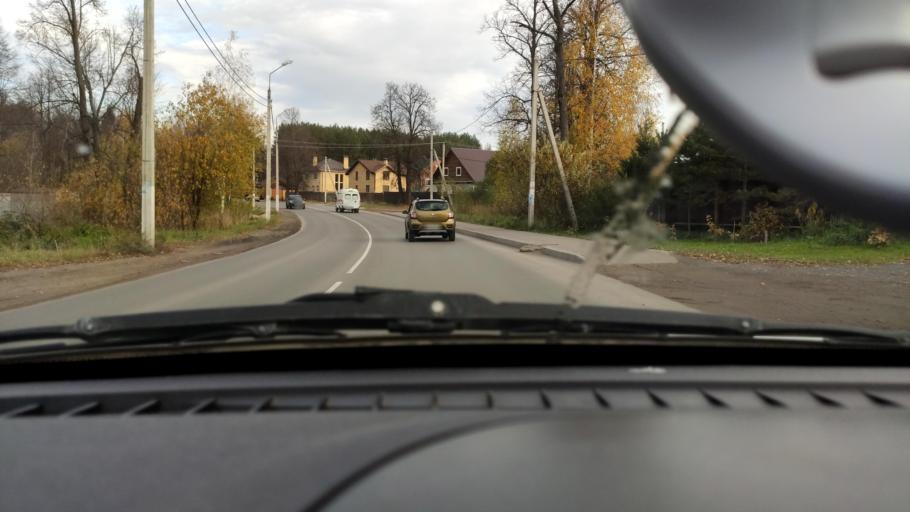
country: RU
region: Perm
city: Perm
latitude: 58.0903
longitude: 56.4035
